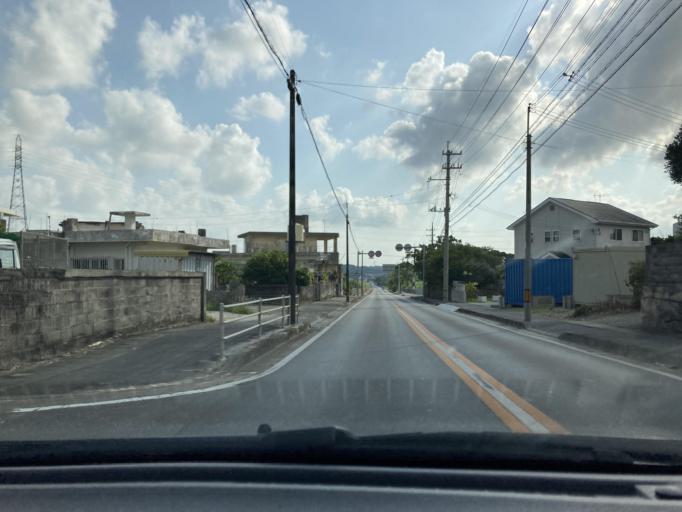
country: JP
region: Okinawa
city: Itoman
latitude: 26.1492
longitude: 127.7077
